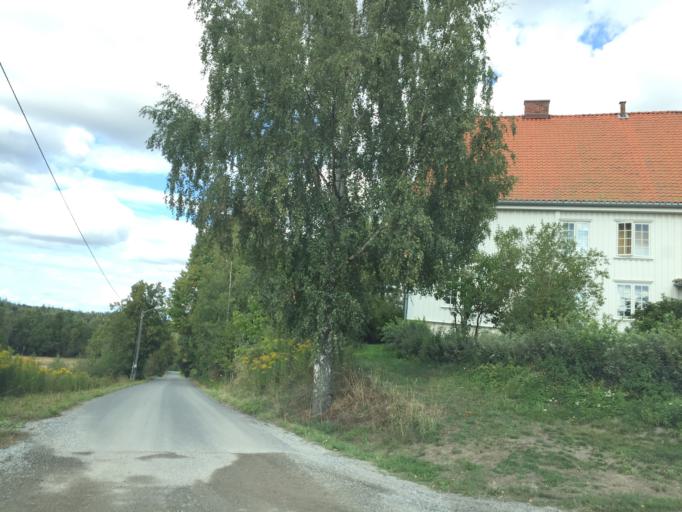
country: NO
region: Ostfold
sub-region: Hobol
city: Elvestad
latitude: 59.6013
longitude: 10.9229
